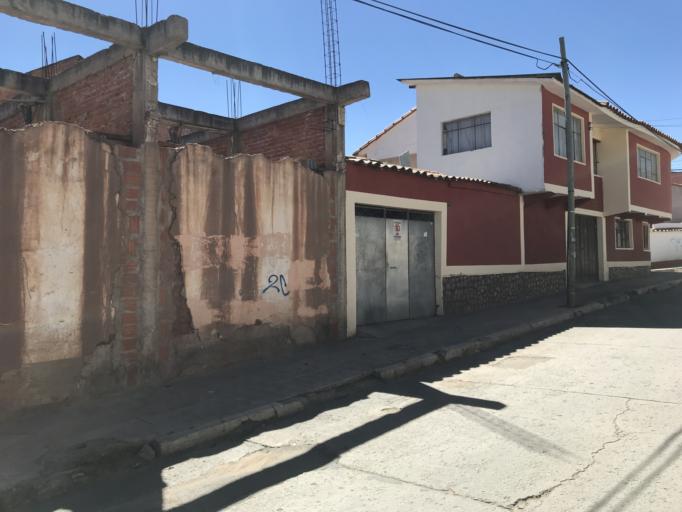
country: BO
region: Chuquisaca
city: Sucre
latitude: -19.0395
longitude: -65.2511
